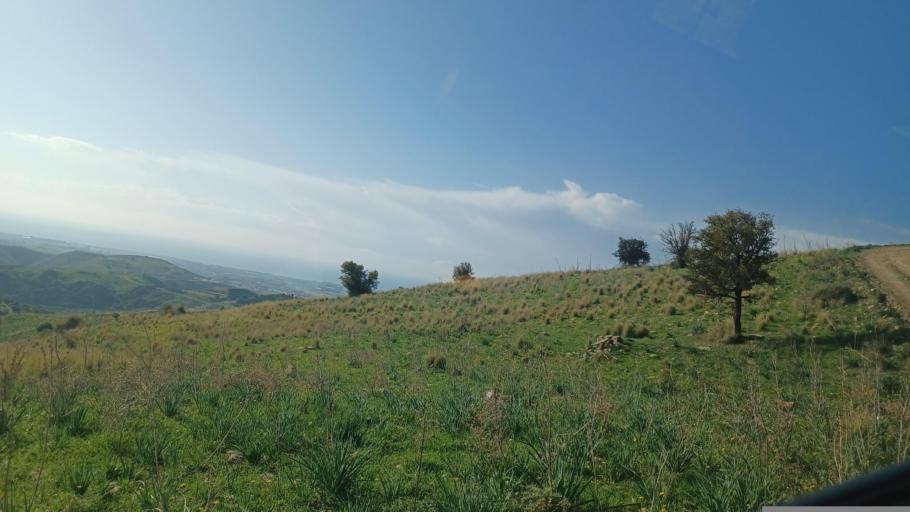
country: CY
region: Pafos
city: Mesogi
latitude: 34.7756
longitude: 32.5445
